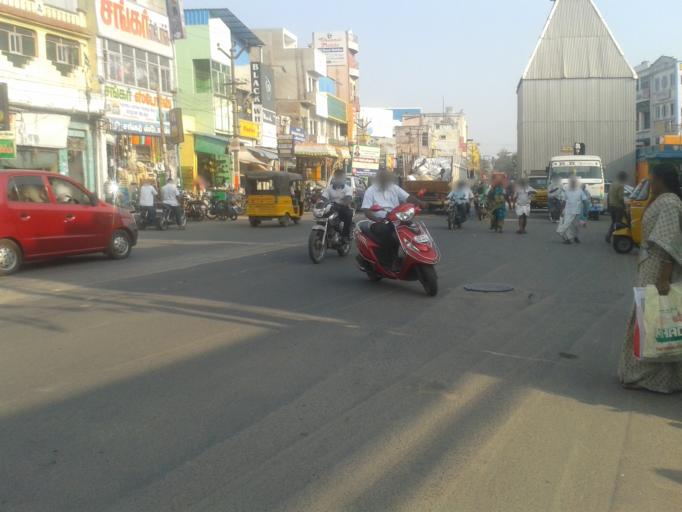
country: IN
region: Tamil Nadu
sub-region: Kancheepuram
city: Kanchipuram
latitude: 12.8256
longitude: 79.7089
